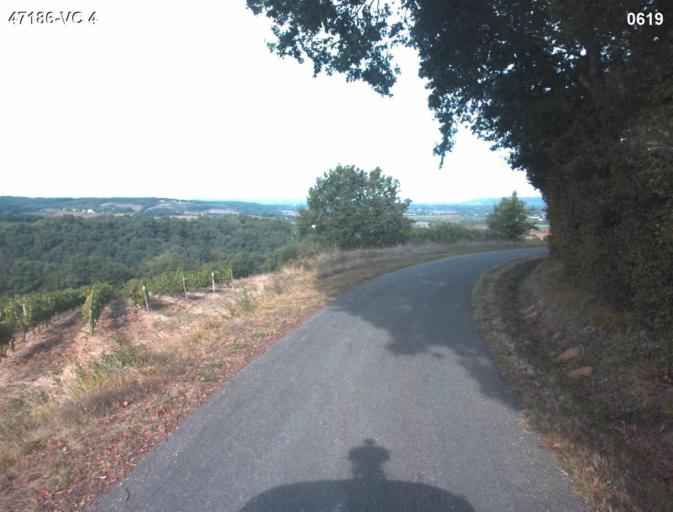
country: FR
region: Aquitaine
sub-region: Departement du Lot-et-Garonne
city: Port-Sainte-Marie
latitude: 44.1992
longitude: 0.4265
